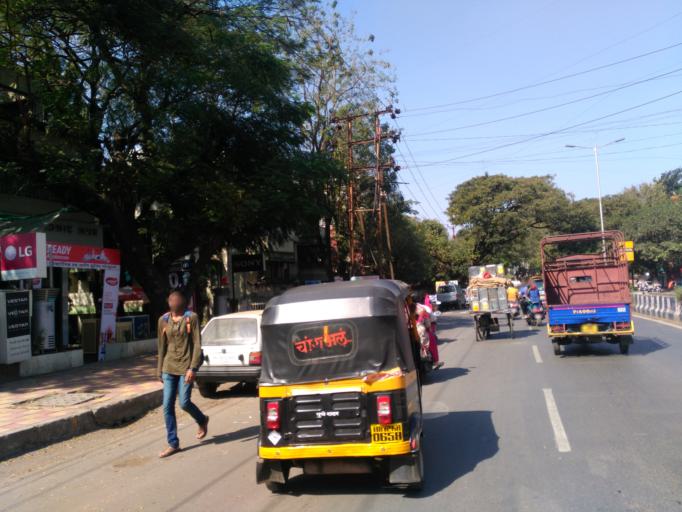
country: IN
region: Maharashtra
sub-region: Pune Division
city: Pune
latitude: 18.4706
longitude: 73.8637
